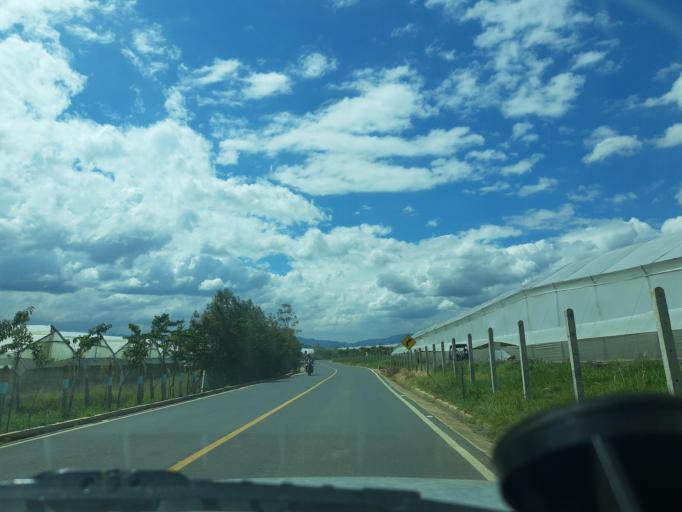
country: CO
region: Boyaca
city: Sutamarchan
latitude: 5.6347
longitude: -73.6008
